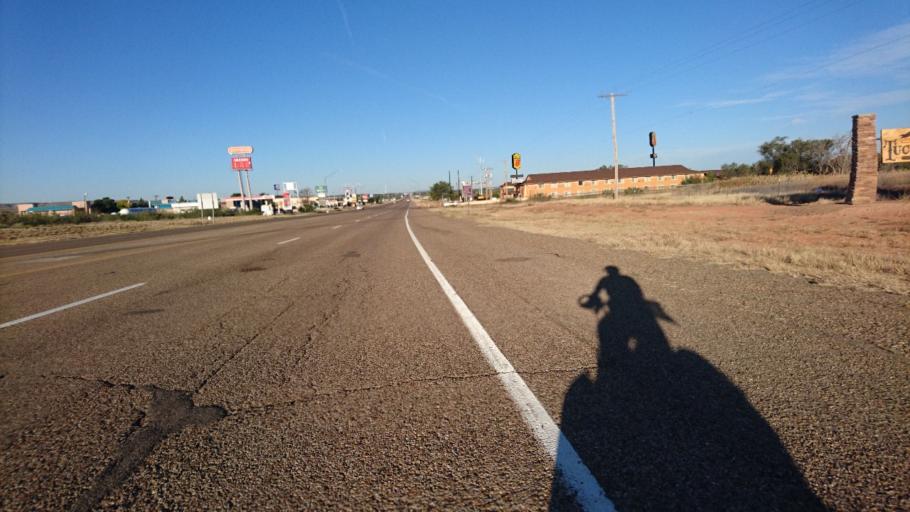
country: US
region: New Mexico
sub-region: Quay County
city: Tucumcari
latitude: 35.1720
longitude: -103.6783
